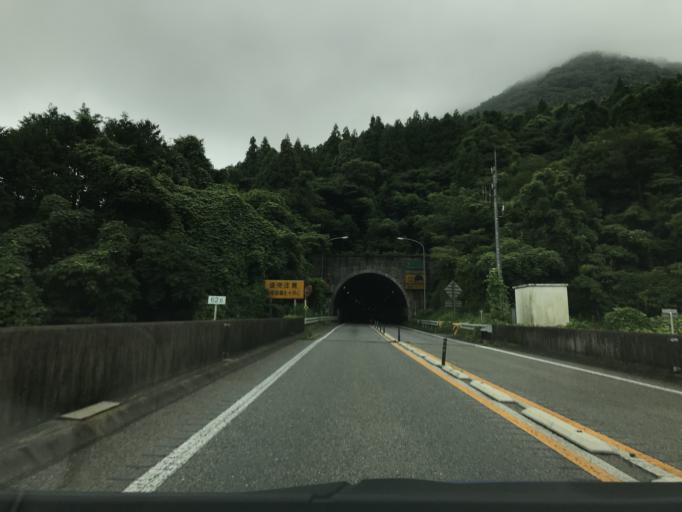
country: JP
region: Oita
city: Bungo-Takada-shi
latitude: 33.4895
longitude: 131.3243
